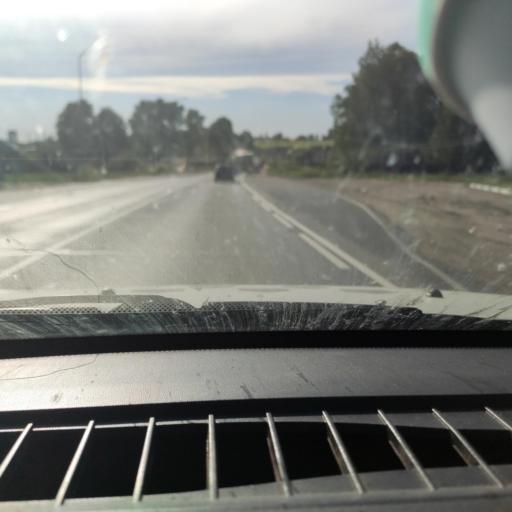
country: RU
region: Kirov
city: Vakhrushi
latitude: 58.6765
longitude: 50.0067
